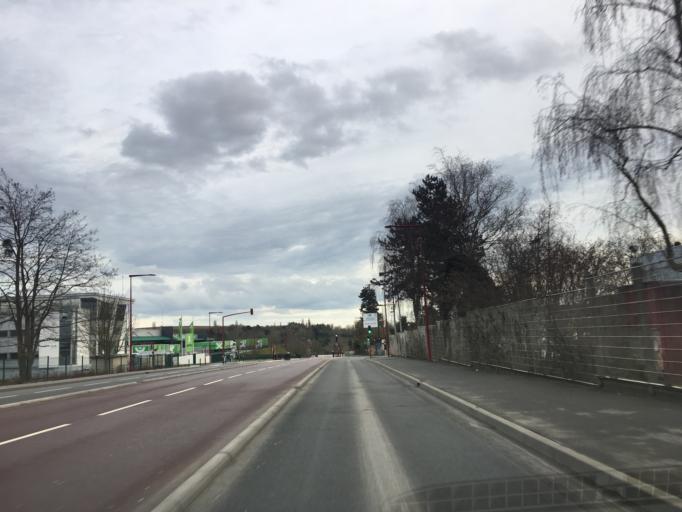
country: FR
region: Ile-de-France
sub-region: Departement du Val-d'Oise
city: Gonesse
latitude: 48.9915
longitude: 2.4561
